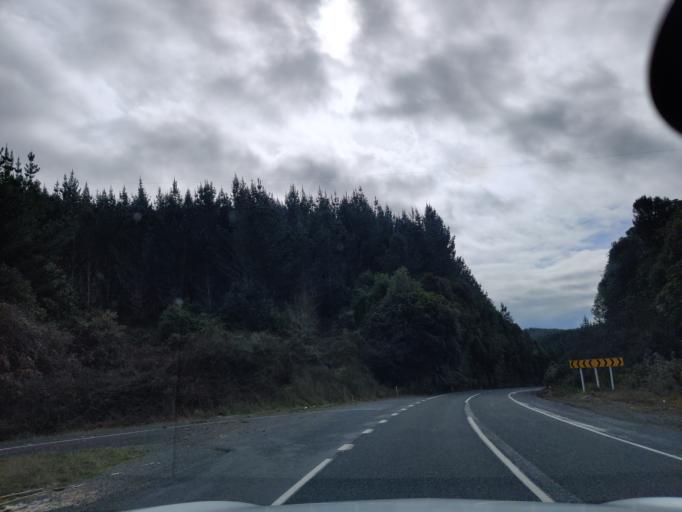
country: NZ
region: Waikato
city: Turangi
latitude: -38.7476
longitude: 175.6758
